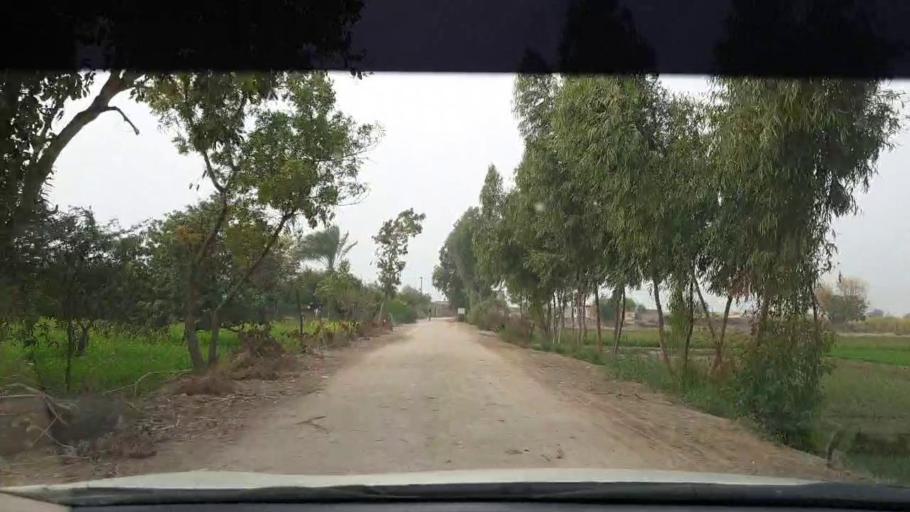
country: PK
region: Sindh
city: Berani
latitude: 25.8661
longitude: 68.7881
